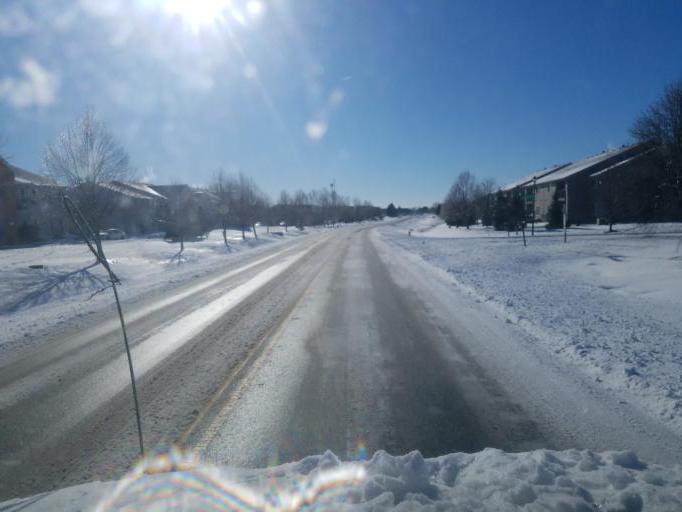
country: US
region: Ohio
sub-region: Delaware County
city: Lewis Center
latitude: 40.1720
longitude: -83.0103
